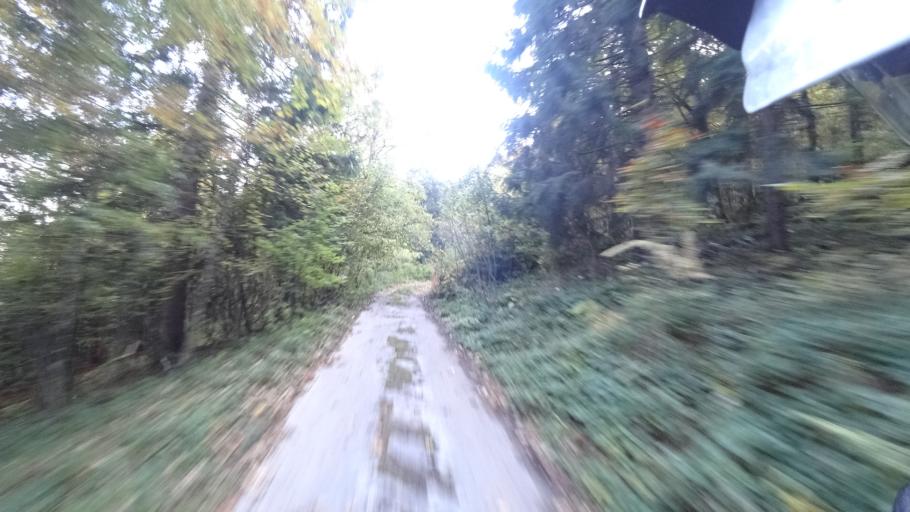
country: HR
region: Karlovacka
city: Plaski
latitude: 44.9734
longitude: 15.4311
